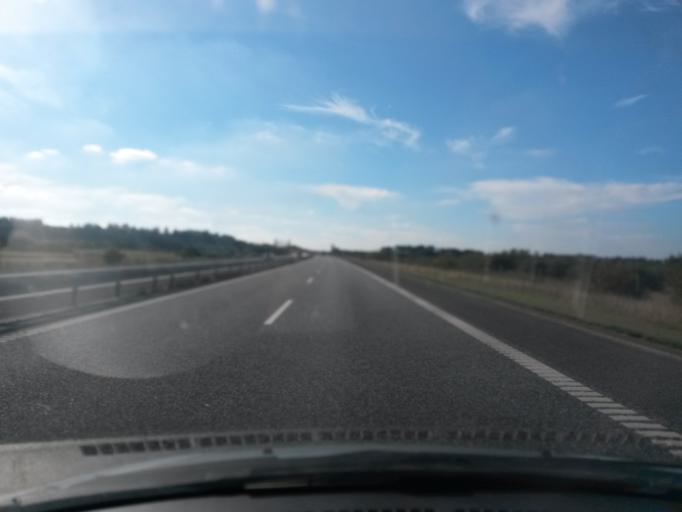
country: DK
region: Central Jutland
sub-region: Ikast-Brande Kommune
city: Bording Kirkeby
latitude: 56.1291
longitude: 9.2130
